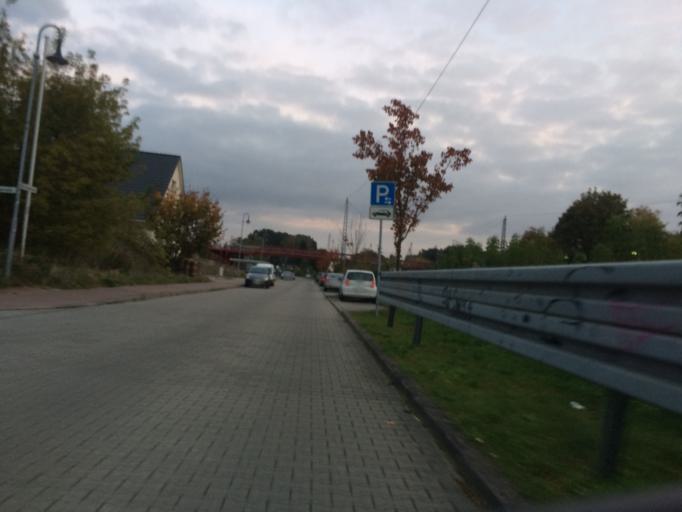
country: DE
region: Brandenburg
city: Glienicke
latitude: 52.6705
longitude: 13.3201
